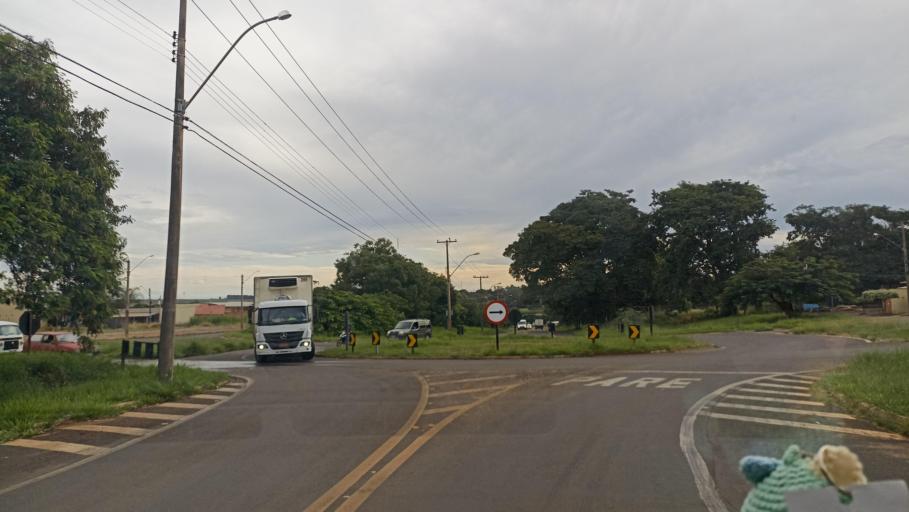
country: BR
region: Sao Paulo
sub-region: Jaboticabal
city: Jaboticabal
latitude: -21.2628
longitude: -48.3384
